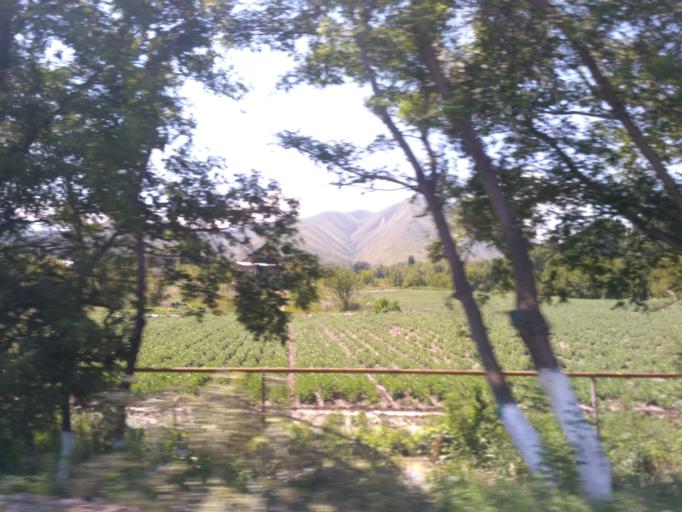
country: KZ
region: Almaty Oblysy
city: Burunday
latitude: 43.1664
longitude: 76.5860
